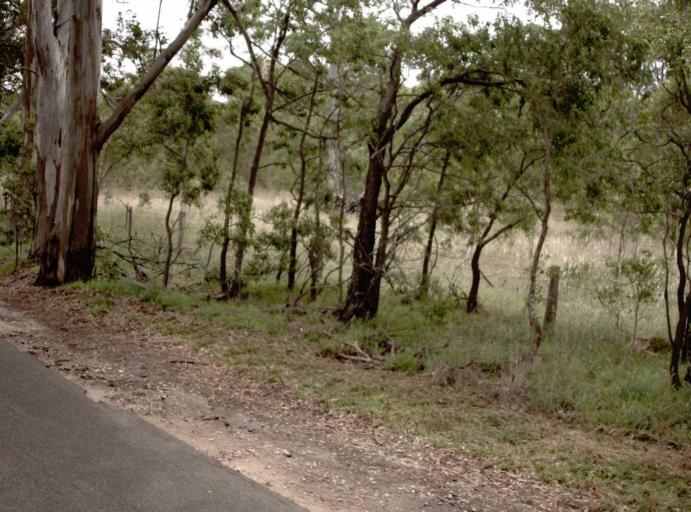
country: AU
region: Victoria
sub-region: Wellington
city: Sale
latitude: -37.8642
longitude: 147.0685
